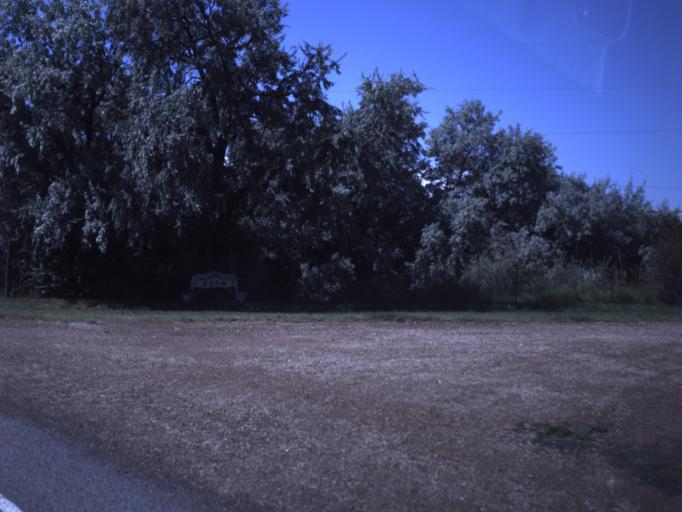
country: US
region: Utah
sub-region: Duchesne County
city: Duchesne
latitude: 40.2701
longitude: -110.2187
